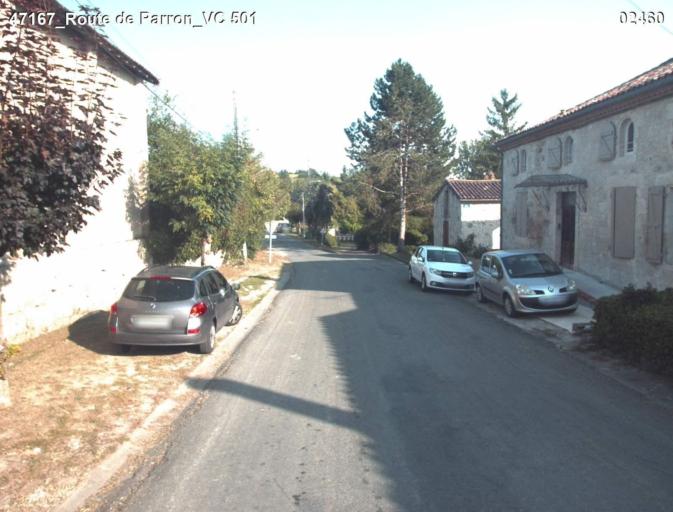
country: FR
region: Aquitaine
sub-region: Departement du Lot-et-Garonne
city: Mezin
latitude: 44.0538
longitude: 0.2607
